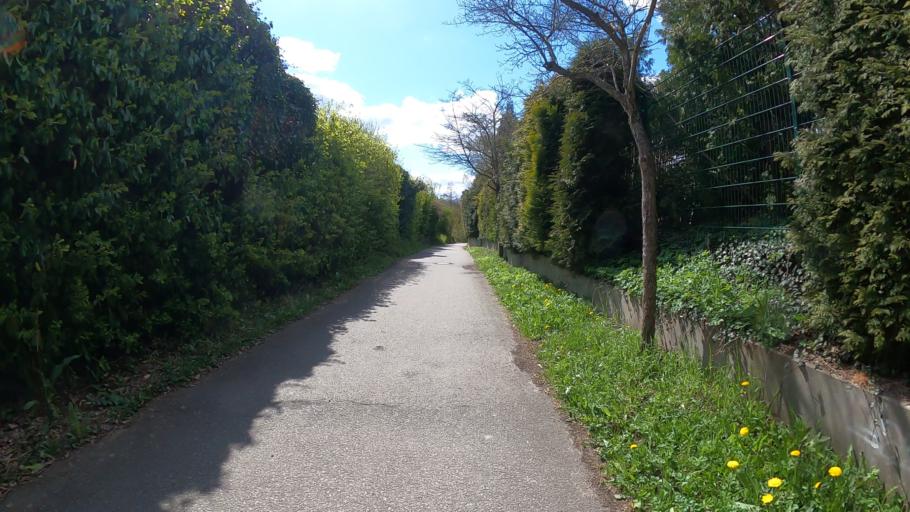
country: DE
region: Schleswig-Holstein
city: Wentorf bei Hamburg
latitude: 53.5032
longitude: 10.2425
